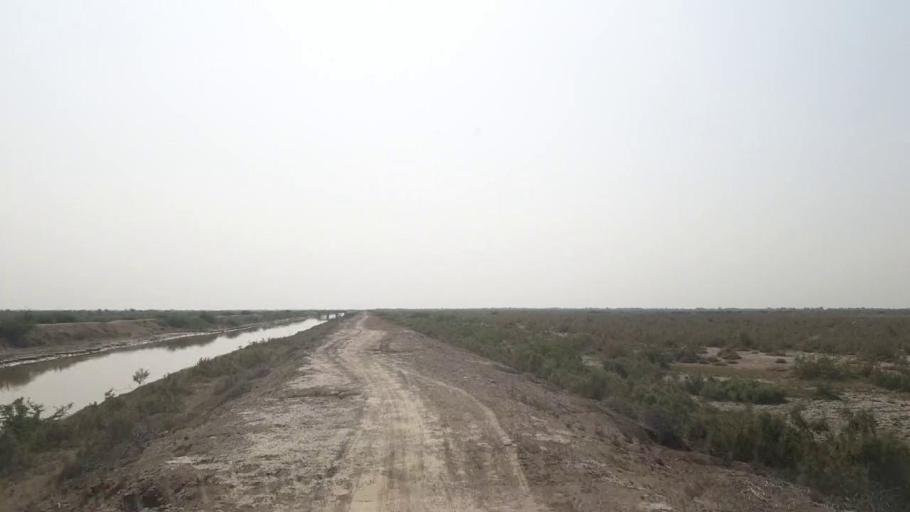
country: PK
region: Sindh
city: Kadhan
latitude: 24.3837
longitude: 68.8991
